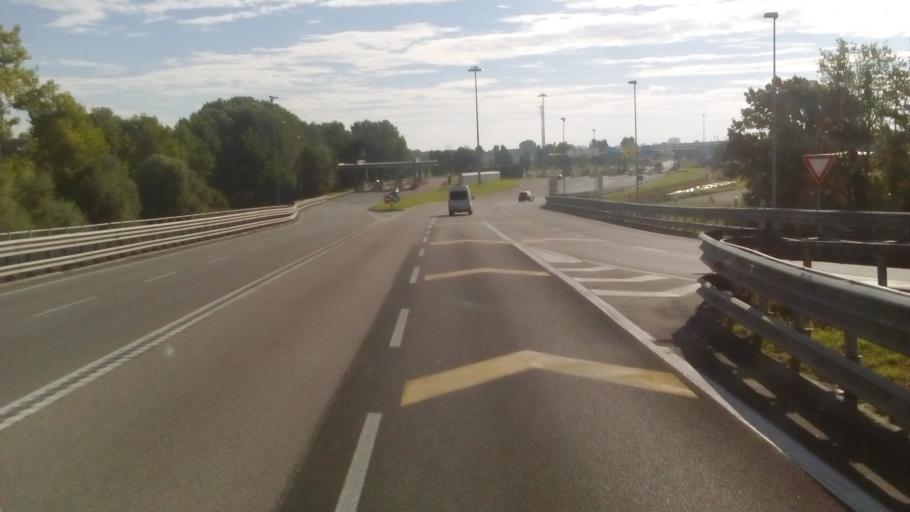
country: IT
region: Lombardy
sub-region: Provincia di Lodi
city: Borgo San Giovanni
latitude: 45.2786
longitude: 9.4467
